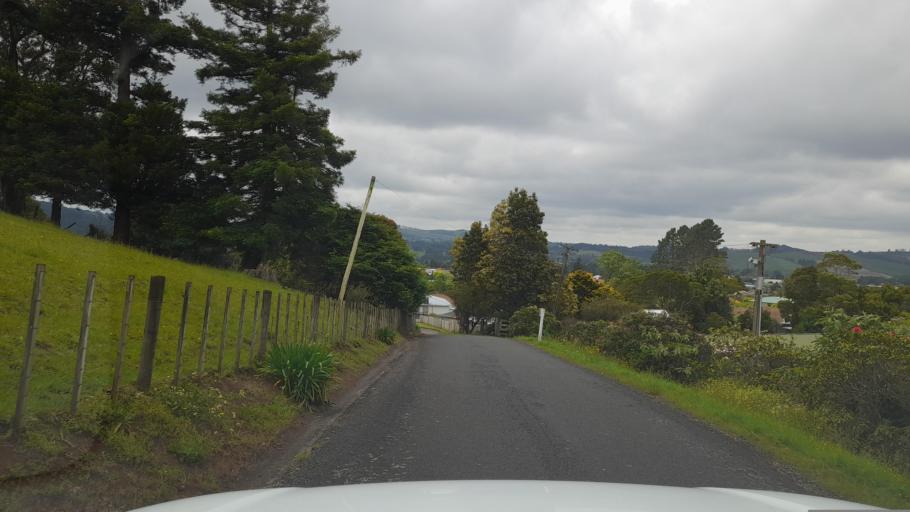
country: NZ
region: Northland
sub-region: Far North District
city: Waimate North
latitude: -35.4103
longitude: 173.7862
